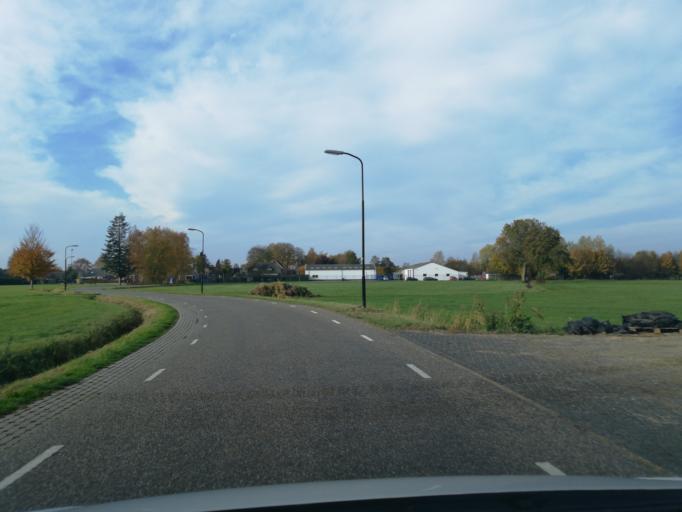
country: NL
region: Gelderland
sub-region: Gemeente Epe
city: Vaassen
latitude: 52.2561
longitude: 5.9945
